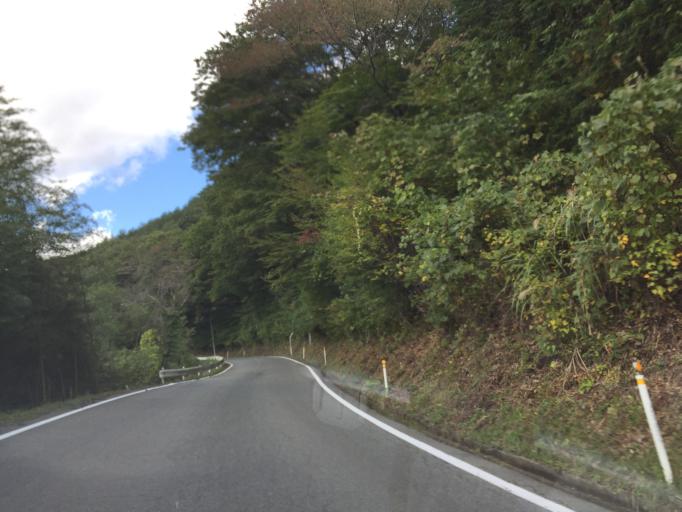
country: JP
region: Fukushima
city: Namie
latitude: 37.5588
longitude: 140.8303
